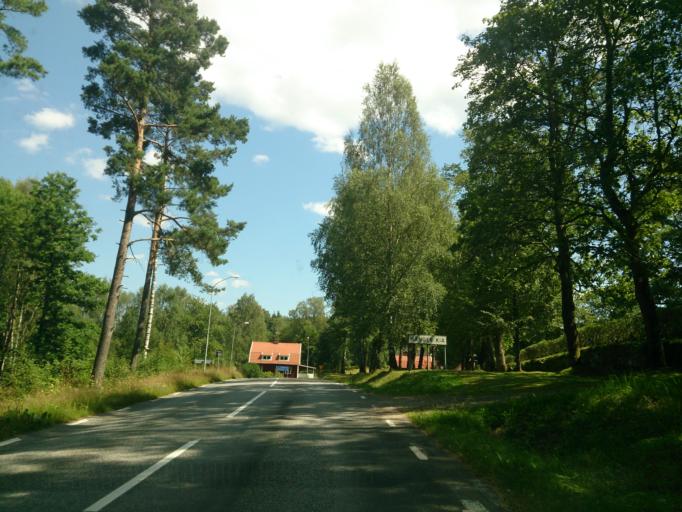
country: SE
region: Joenkoeping
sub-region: Varnamo Kommun
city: Varnamo
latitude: 57.0850
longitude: 13.9593
